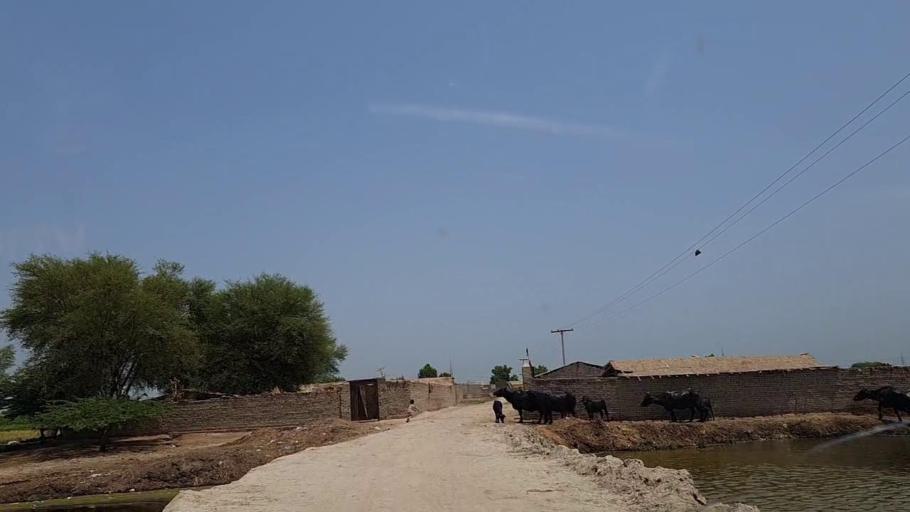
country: PK
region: Sindh
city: Ghotki
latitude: 27.9944
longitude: 69.3644
